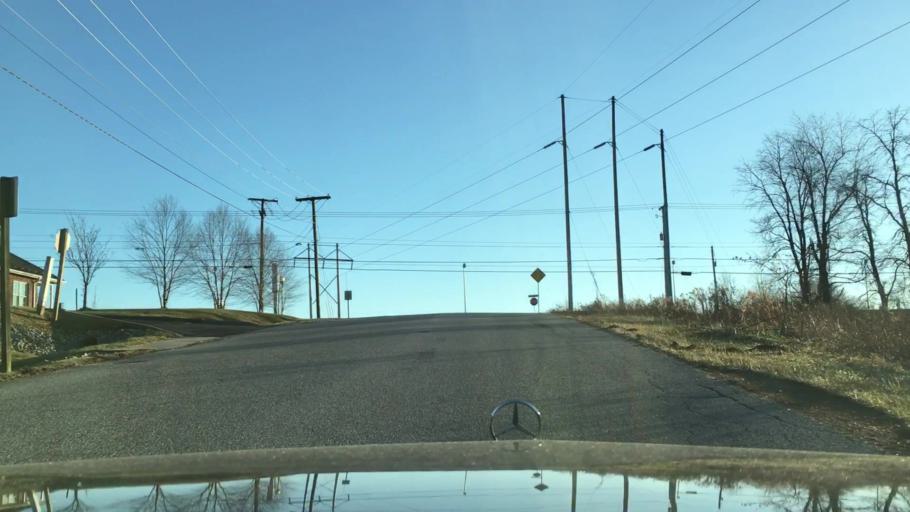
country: US
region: Virginia
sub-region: Montgomery County
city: Merrimac
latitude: 37.1637
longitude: -80.4436
